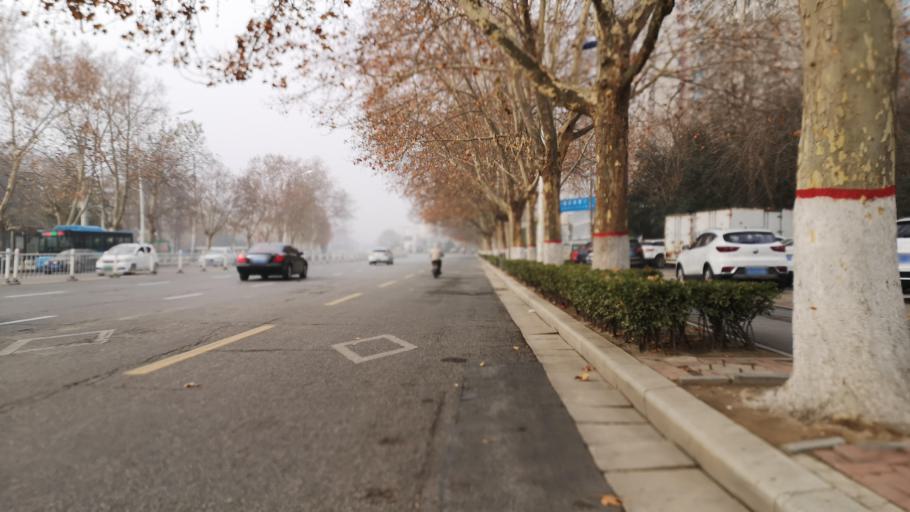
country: CN
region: Henan Sheng
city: Zhongyuanlu
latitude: 35.7803
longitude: 115.0478
